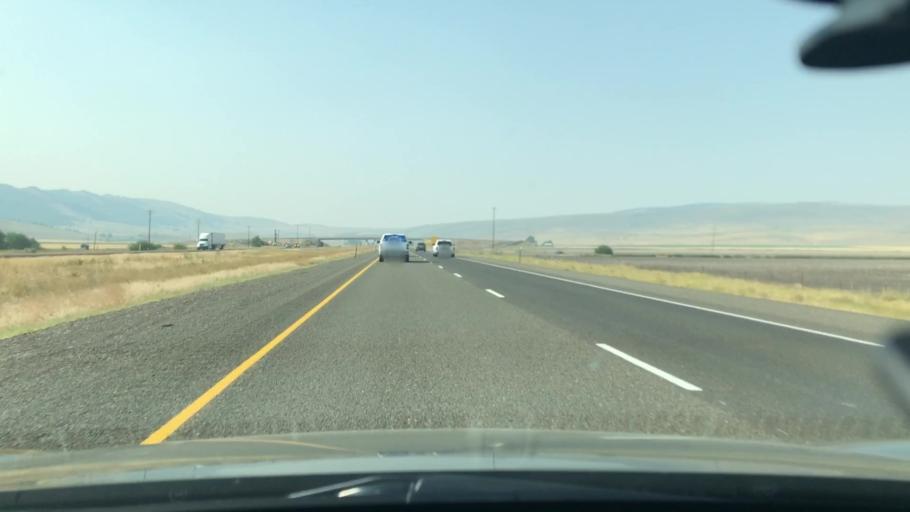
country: US
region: Oregon
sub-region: Union County
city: Union
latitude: 45.0900
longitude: -117.9504
